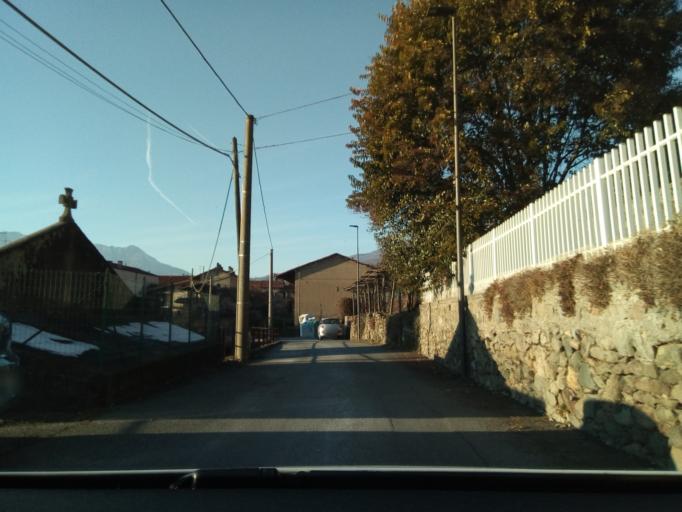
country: IT
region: Piedmont
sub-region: Provincia di Torino
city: Burolo
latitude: 45.4811
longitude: 7.9358
